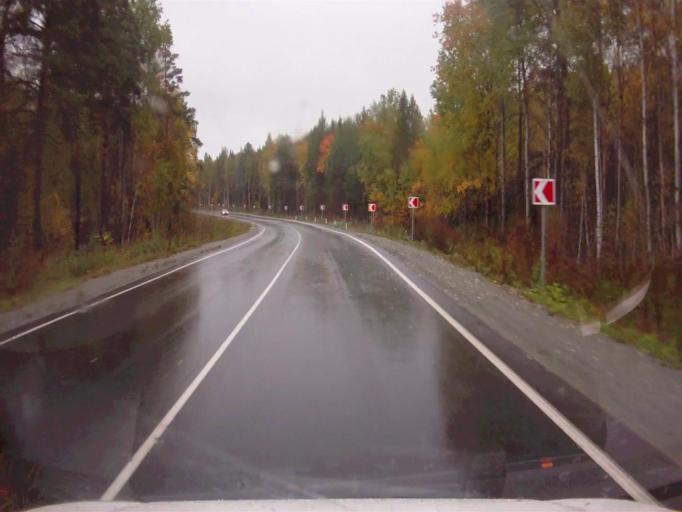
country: RU
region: Chelyabinsk
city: Tayginka
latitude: 55.6328
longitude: 60.5999
